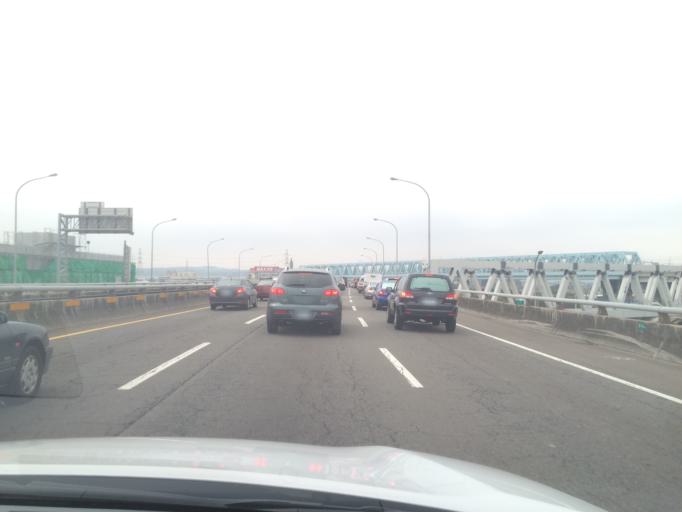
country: TW
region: Taiwan
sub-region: Changhua
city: Chang-hua
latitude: 24.1106
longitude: 120.6196
